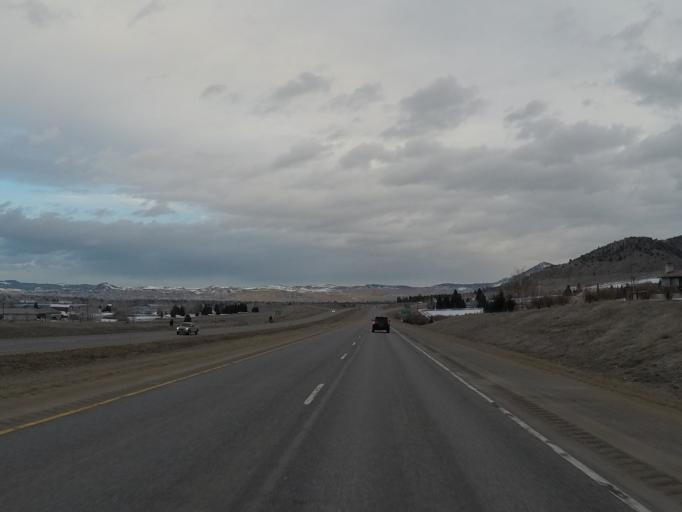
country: US
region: Montana
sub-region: Silver Bow County
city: Butte
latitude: 45.9531
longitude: -112.4680
